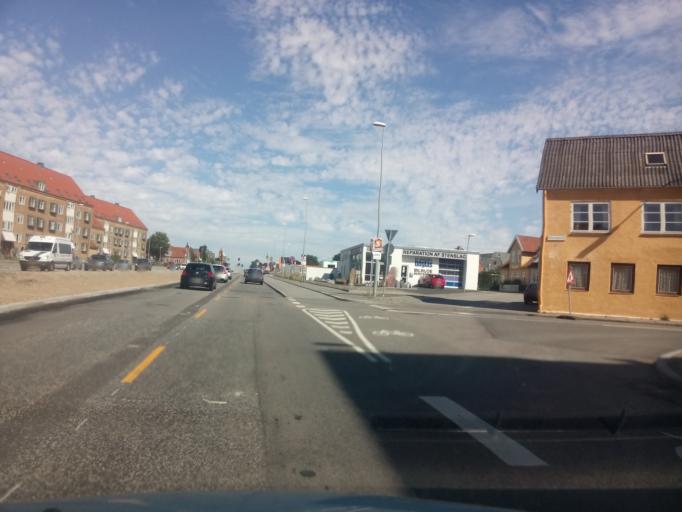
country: DK
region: Central Jutland
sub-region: Arhus Kommune
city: Arhus
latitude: 56.1766
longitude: 10.2016
